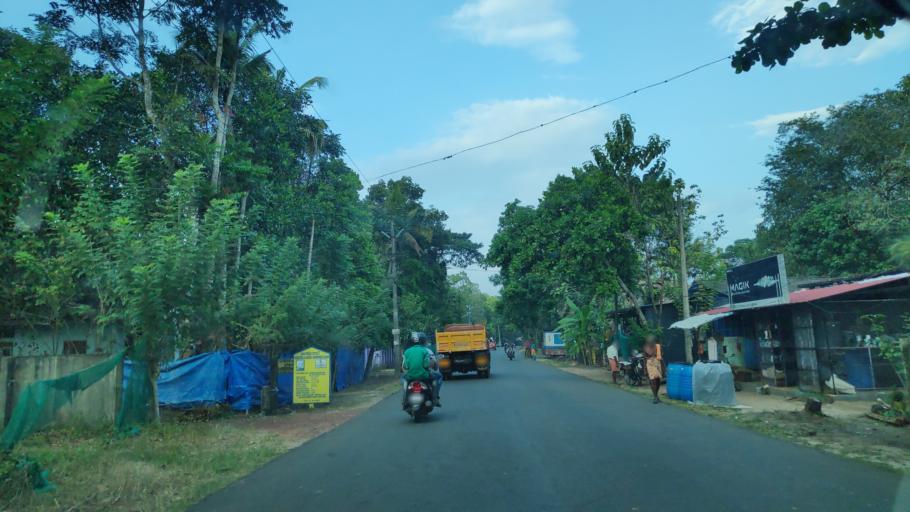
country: IN
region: Kerala
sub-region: Alappuzha
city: Shertallai
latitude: 9.6572
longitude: 76.3763
